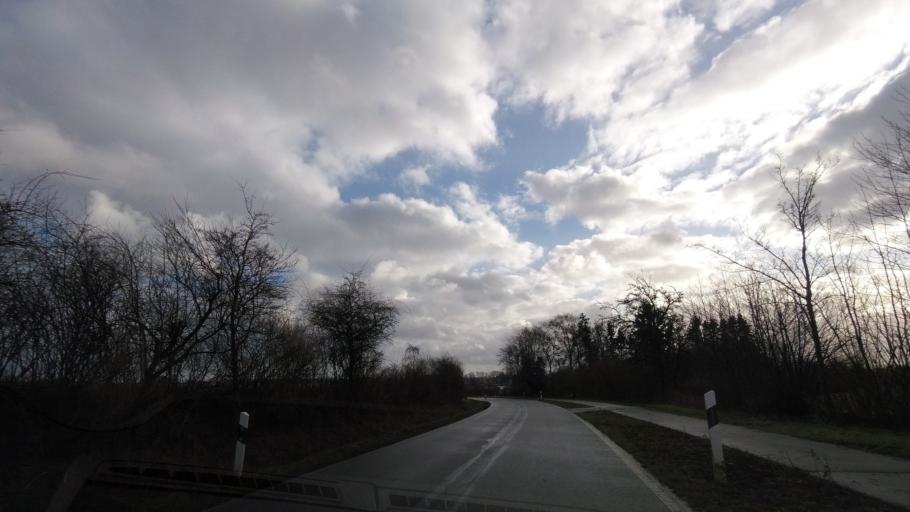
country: DE
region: Schleswig-Holstein
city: Grodersby
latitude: 54.6354
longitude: 9.9224
